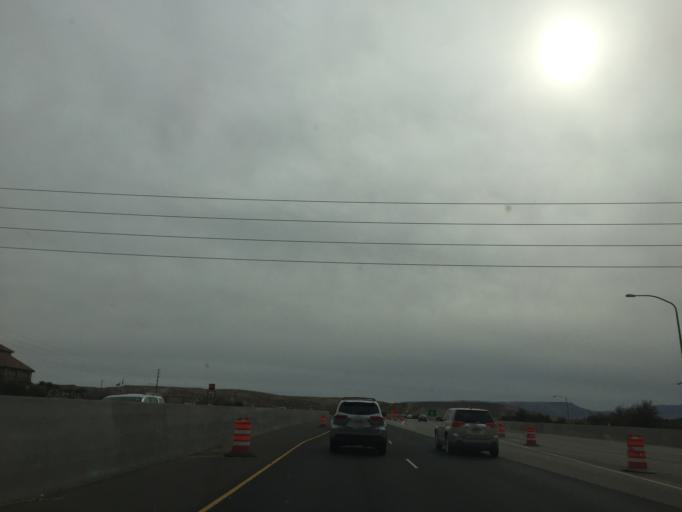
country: US
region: Utah
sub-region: Washington County
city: Saint George
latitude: 37.0653
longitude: -113.5841
